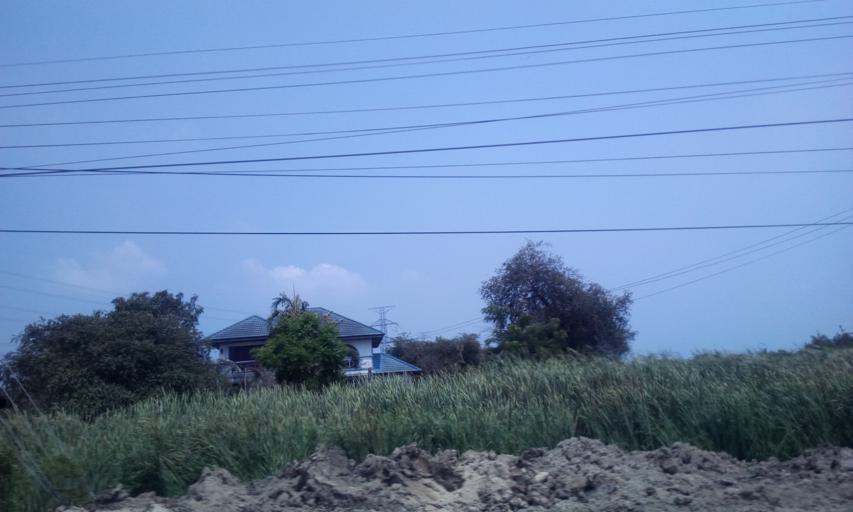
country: TH
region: Chachoengsao
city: Ban Pho
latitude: 13.5759
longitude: 101.1256
